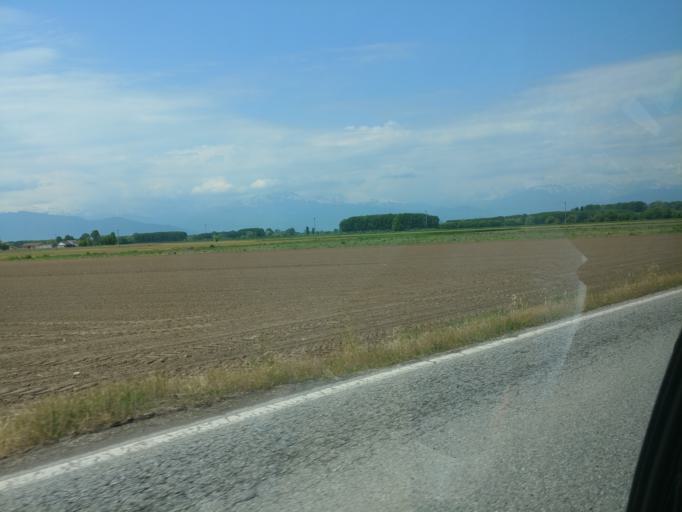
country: IT
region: Piedmont
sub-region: Provincia di Cuneo
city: Moretta
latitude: 44.7721
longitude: 7.5236
